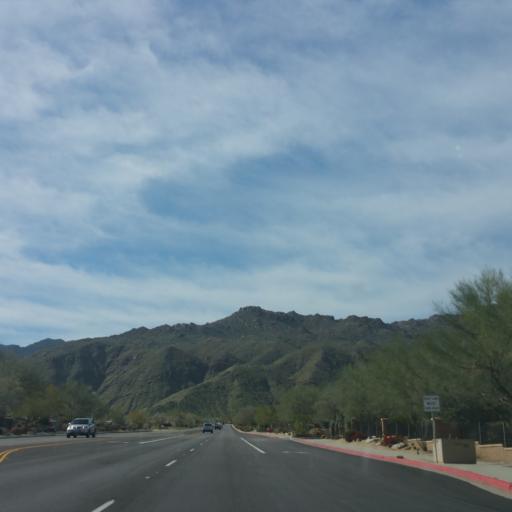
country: US
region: California
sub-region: Riverside County
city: Palm Desert
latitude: 33.6787
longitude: -116.4069
